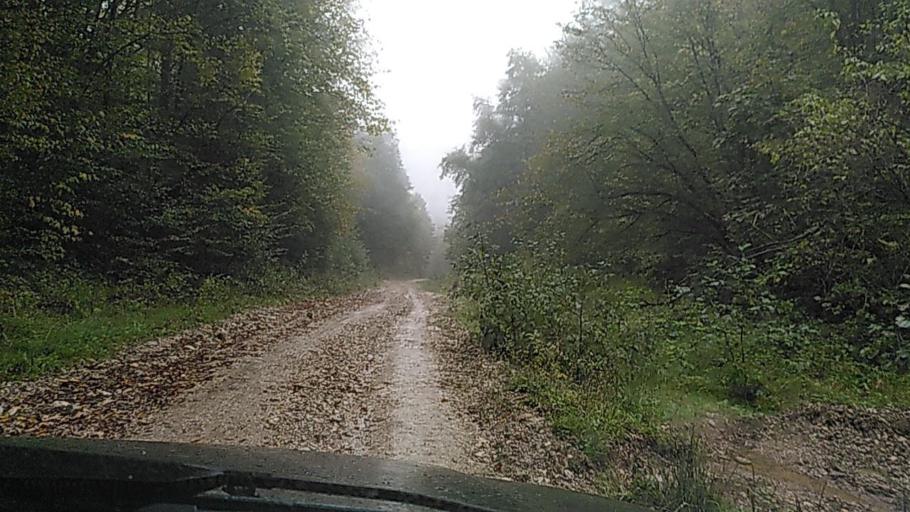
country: RU
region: Kabardino-Balkariya
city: Belaya Rechka
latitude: 43.3644
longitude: 43.4169
